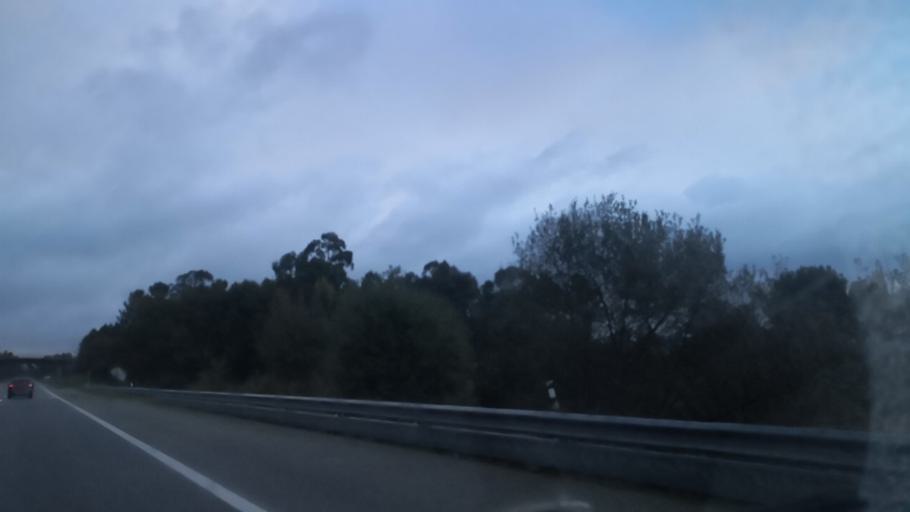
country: PT
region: Braga
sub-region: Vila Verde
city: Prado
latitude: 41.6601
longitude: -8.5482
